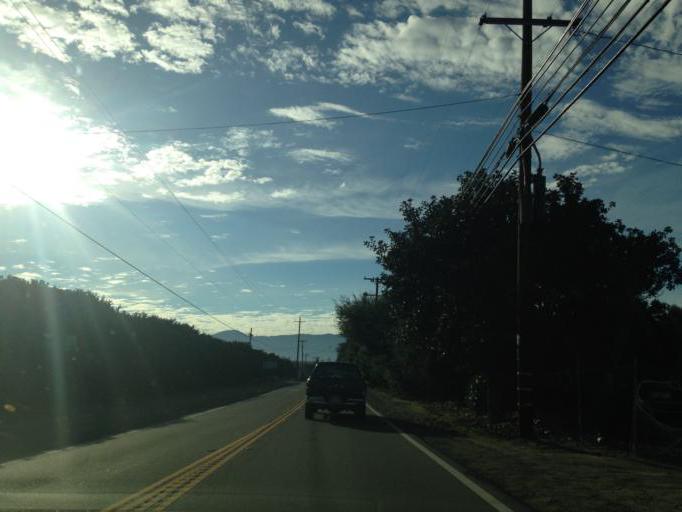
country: US
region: California
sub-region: San Diego County
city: Valley Center
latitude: 33.3290
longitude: -117.0004
